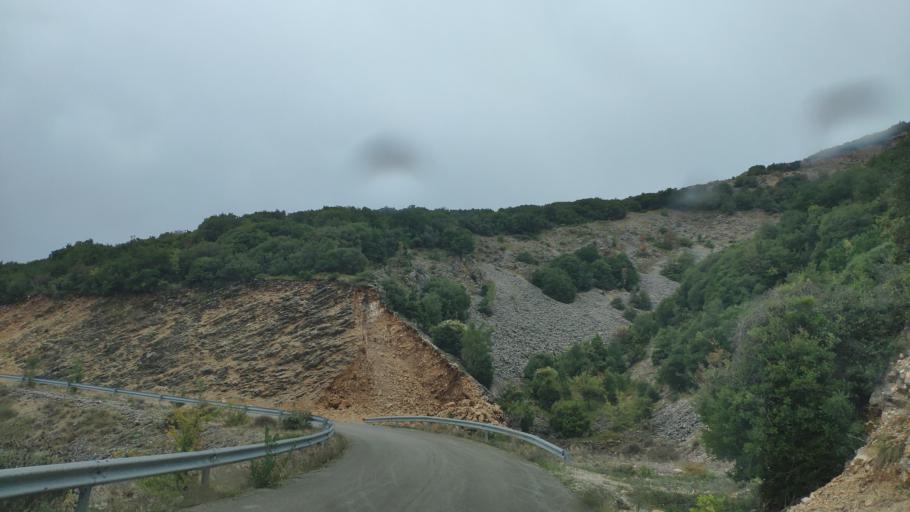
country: GR
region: Epirus
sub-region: Nomos Thesprotias
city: Paramythia
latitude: 39.4564
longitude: 20.6681
